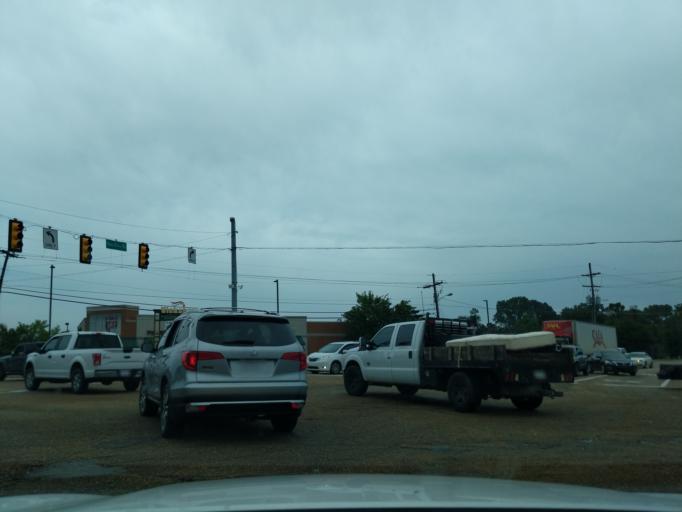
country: US
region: Mississippi
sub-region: Warren County
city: Vicksburg
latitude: 32.3153
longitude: -90.8764
